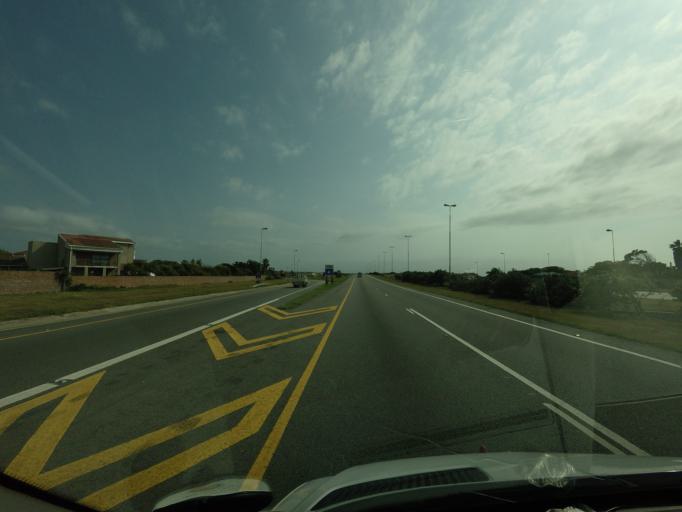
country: ZA
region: Eastern Cape
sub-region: Nelson Mandela Bay Metropolitan Municipality
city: Port Elizabeth
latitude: -33.8534
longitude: 25.6344
